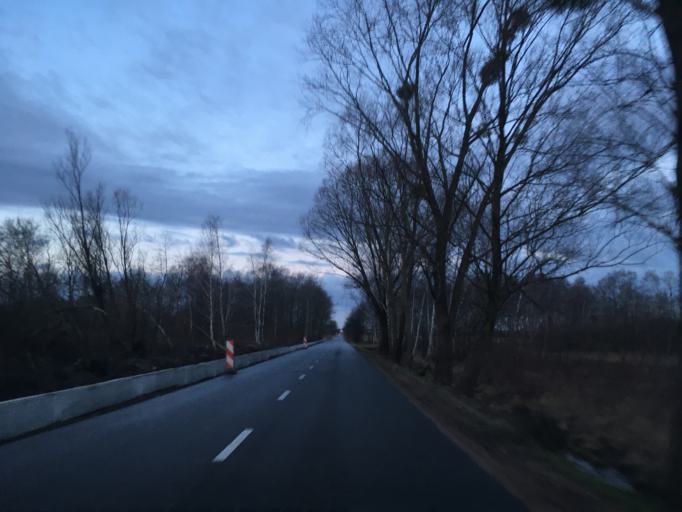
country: PL
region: Masovian Voivodeship
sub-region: Powiat grodziski
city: Podkowa Lesna
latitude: 52.0805
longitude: 20.7440
